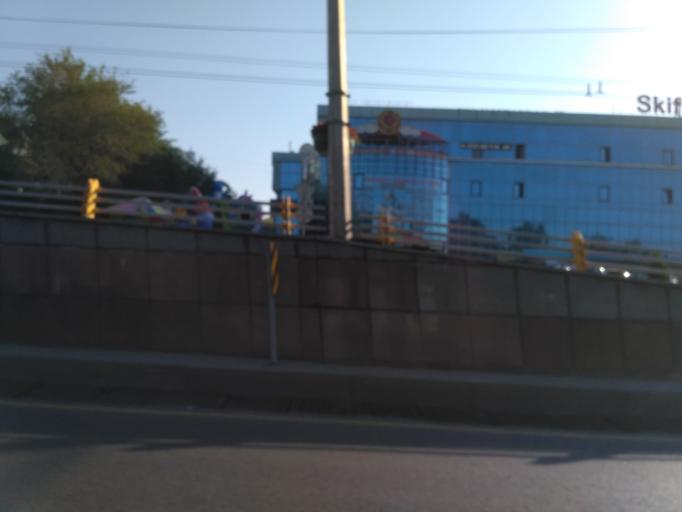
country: KZ
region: Almaty Qalasy
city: Almaty
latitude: 43.2177
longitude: 76.8533
